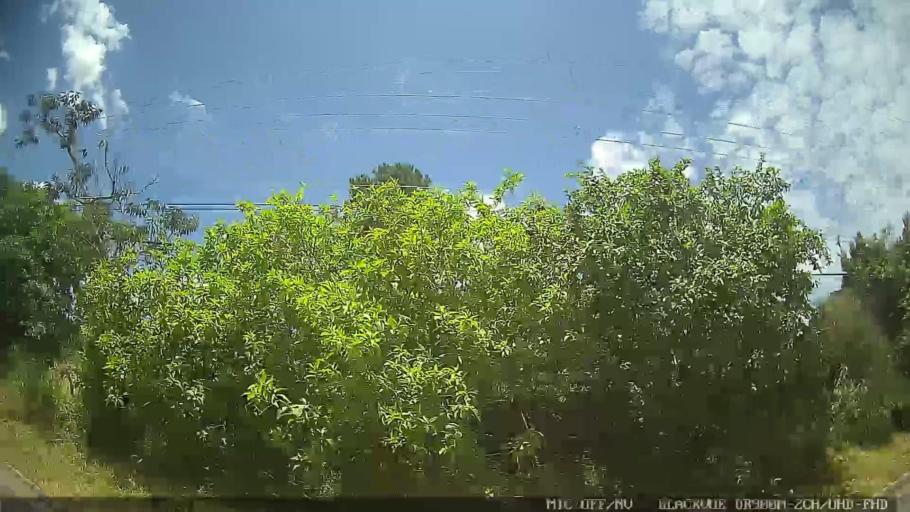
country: BR
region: Sao Paulo
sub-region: Santa Branca
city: Santa Branca
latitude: -23.5242
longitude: -45.8744
